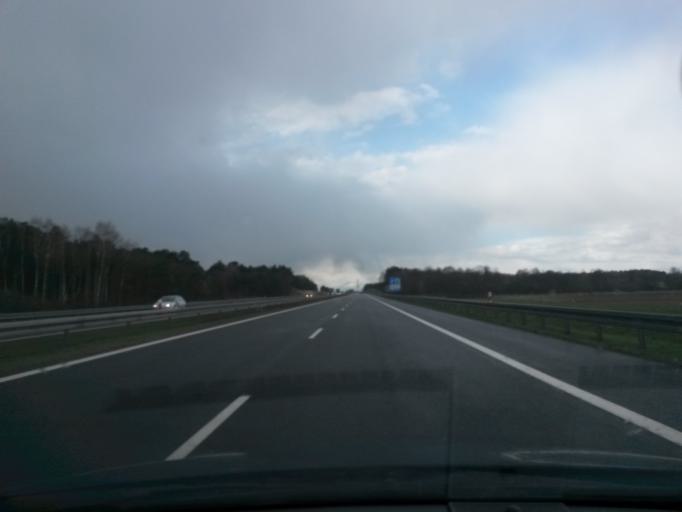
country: PL
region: Greater Poland Voivodeship
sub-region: Powiat koninski
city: Stare Miasto
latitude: 52.1764
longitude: 18.1385
